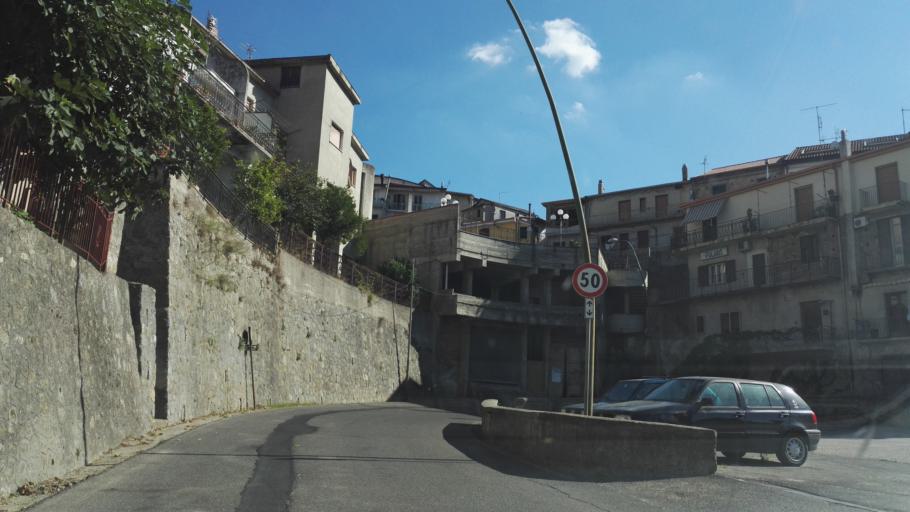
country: IT
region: Calabria
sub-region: Provincia di Vibo-Valentia
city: Sorianello
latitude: 38.5929
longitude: 16.2315
